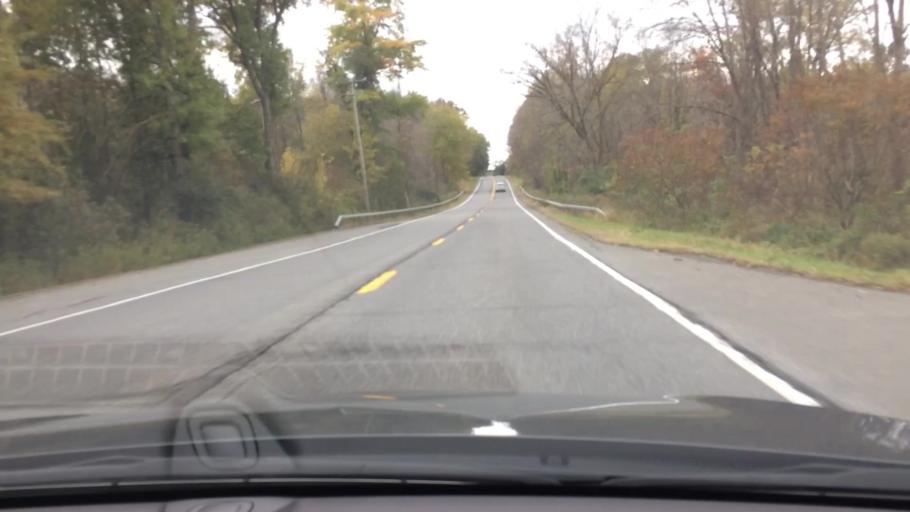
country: US
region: New York
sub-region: Columbia County
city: Kinderhook
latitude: 42.3737
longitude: -73.6964
